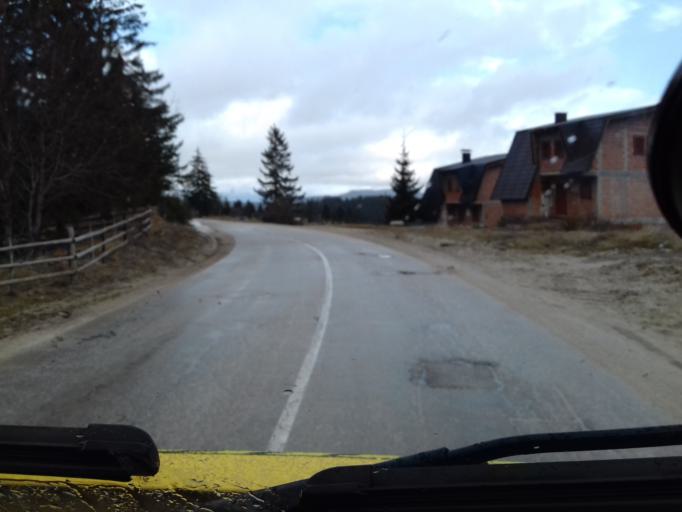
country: BA
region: Federation of Bosnia and Herzegovina
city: Turbe
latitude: 44.3149
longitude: 17.5580
